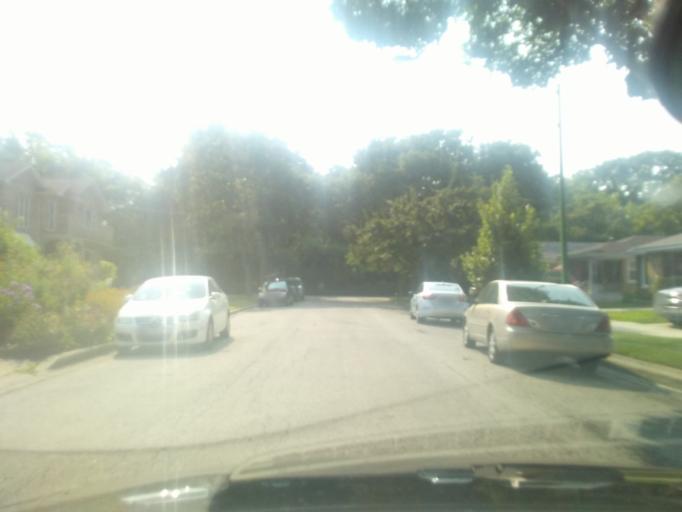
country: US
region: Illinois
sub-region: Cook County
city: Lincolnwood
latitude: 41.9963
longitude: -87.7378
